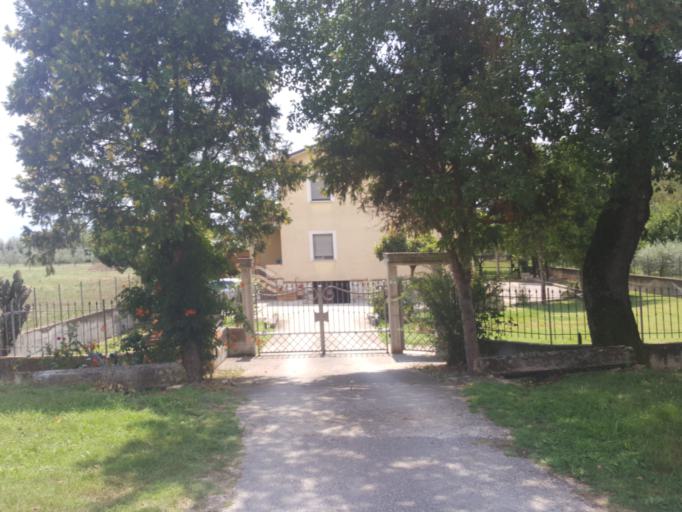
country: IT
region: Latium
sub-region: Provincia di Frosinone
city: Aquino
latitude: 41.5020
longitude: 13.6840
